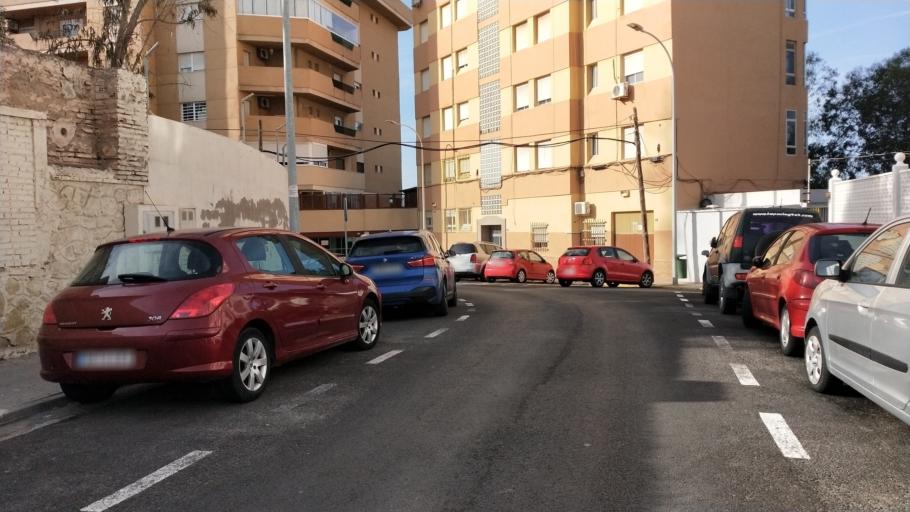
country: ES
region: Melilla
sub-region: Melilla
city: Melilla
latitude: 35.2870
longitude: -2.9479
